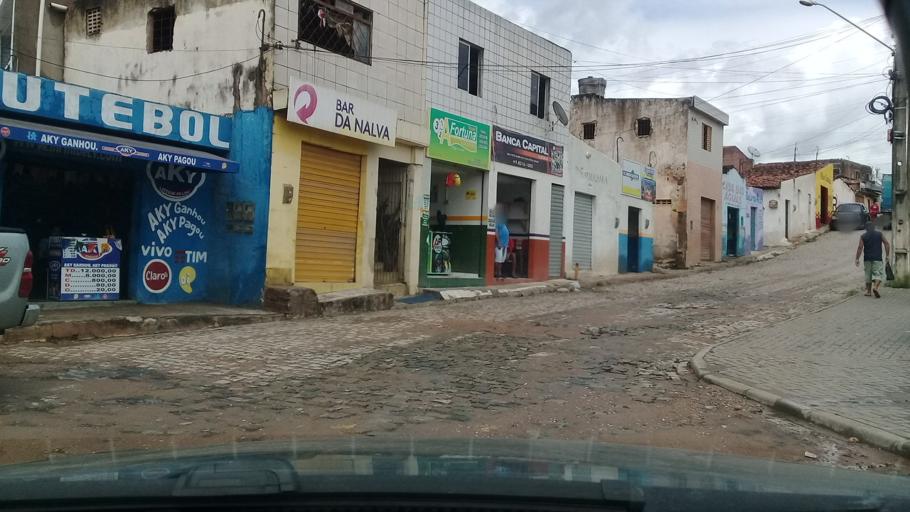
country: BR
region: Pernambuco
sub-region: Vitoria De Santo Antao
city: Vitoria de Santo Antao
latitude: -8.1261
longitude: -35.2823
